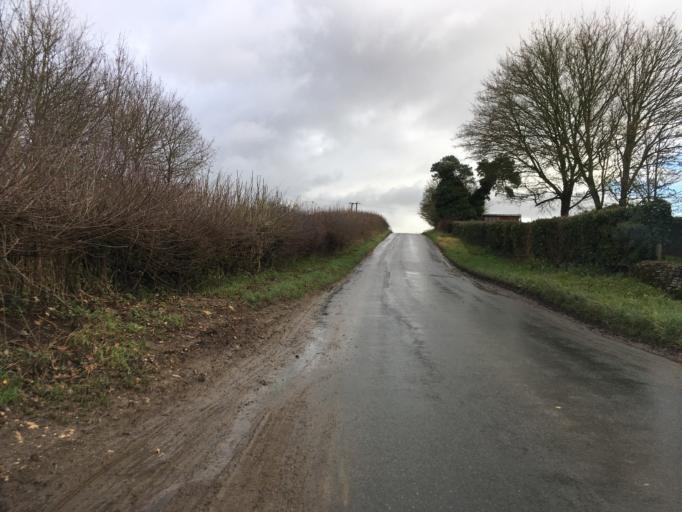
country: GB
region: England
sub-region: Gloucestershire
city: Tetbury
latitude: 51.6330
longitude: -2.1277
